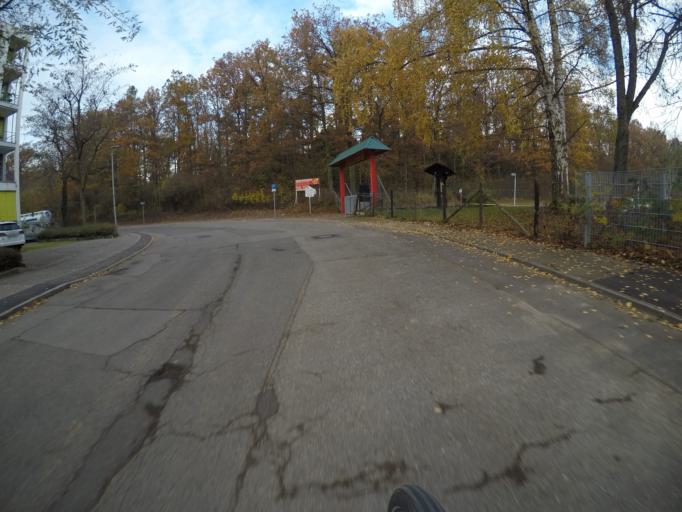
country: DE
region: Baden-Wuerttemberg
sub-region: Regierungsbezirk Stuttgart
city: Leinfelden-Echterdingen
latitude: 48.7096
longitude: 9.1722
